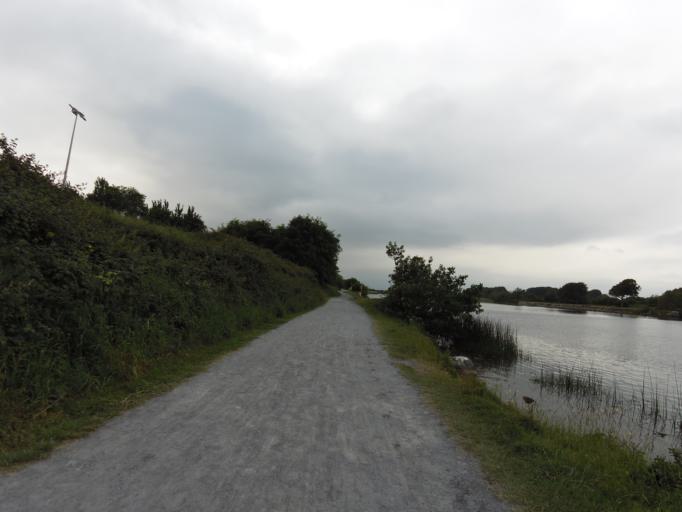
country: IE
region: Connaught
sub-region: County Galway
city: Gaillimh
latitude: 53.2949
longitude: -9.0735
